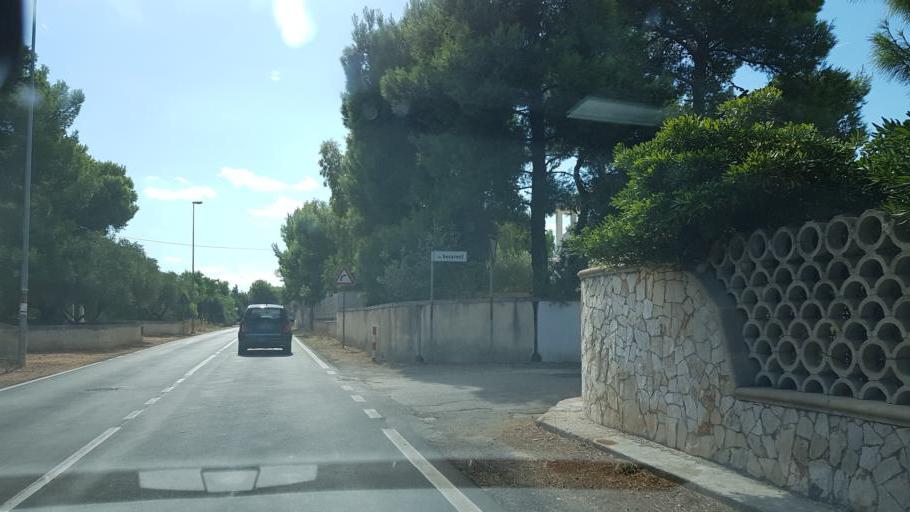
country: IT
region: Apulia
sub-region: Provincia di Lecce
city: Porto Cesareo
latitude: 40.2449
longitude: 17.9138
